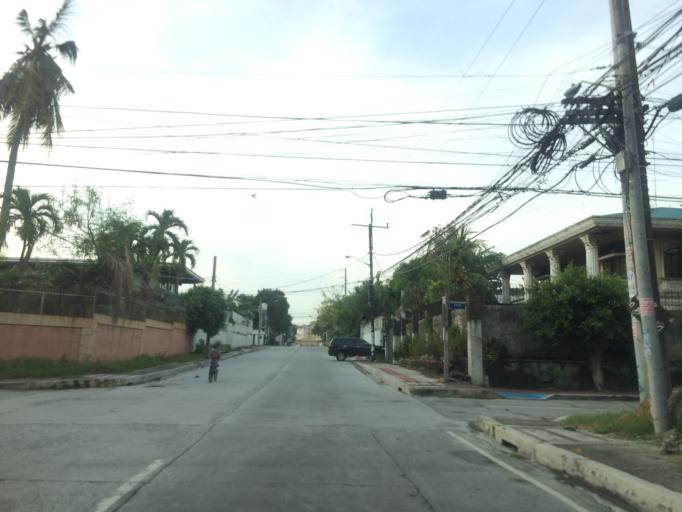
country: PH
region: Calabarzon
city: Del Monte
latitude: 14.6308
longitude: 121.0055
